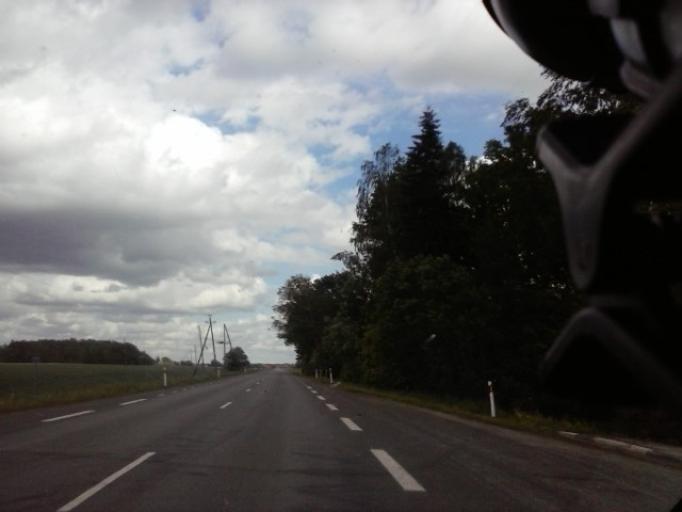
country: EE
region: Jogevamaa
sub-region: Poltsamaa linn
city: Poltsamaa
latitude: 58.6365
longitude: 25.8357
